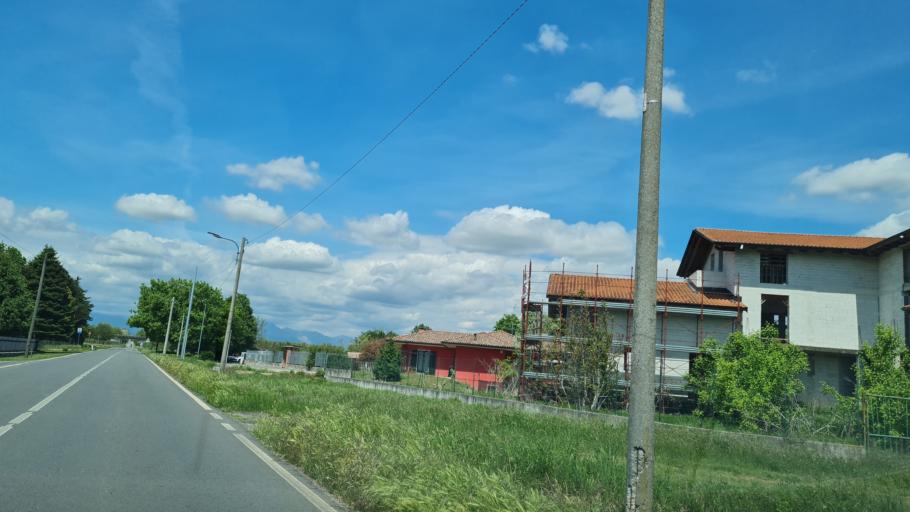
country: IT
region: Piedmont
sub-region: Provincia di Novara
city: Sillavengo
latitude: 45.5228
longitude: 8.4382
